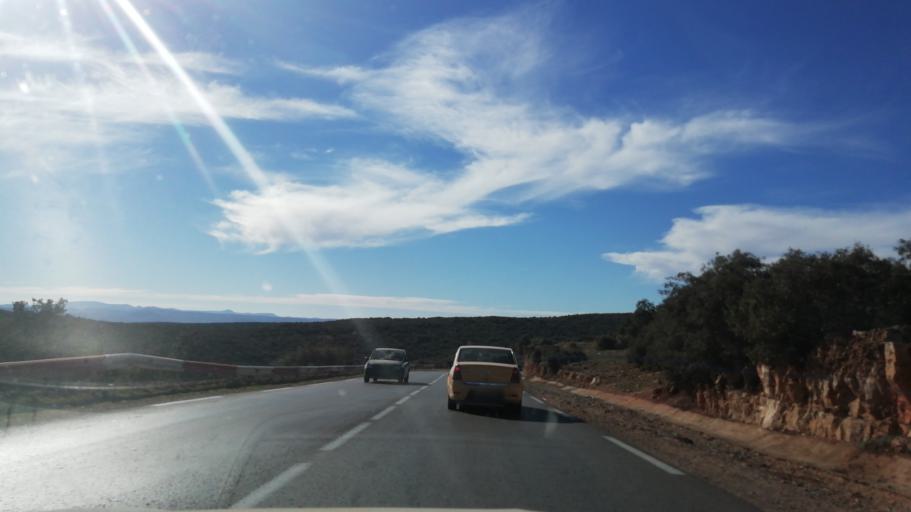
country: DZ
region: Tlemcen
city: Sebdou
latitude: 34.7480
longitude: -1.3459
